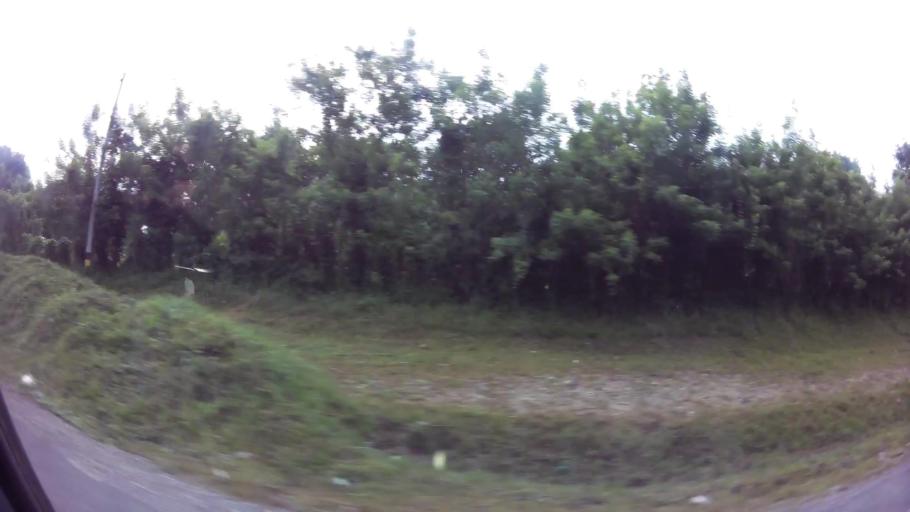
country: HN
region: Yoro
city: Toyos
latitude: 15.5191
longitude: -87.6622
